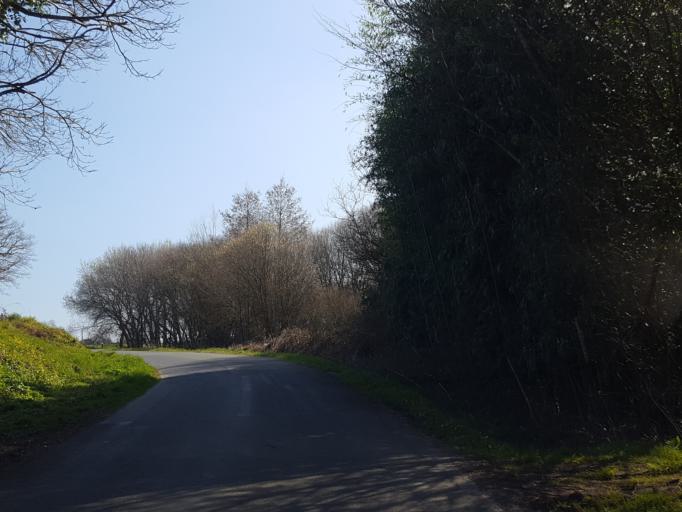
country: FR
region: Pays de la Loire
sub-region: Departement de la Vendee
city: La Chaize-le-Vicomte
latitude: 46.6578
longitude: -1.3031
